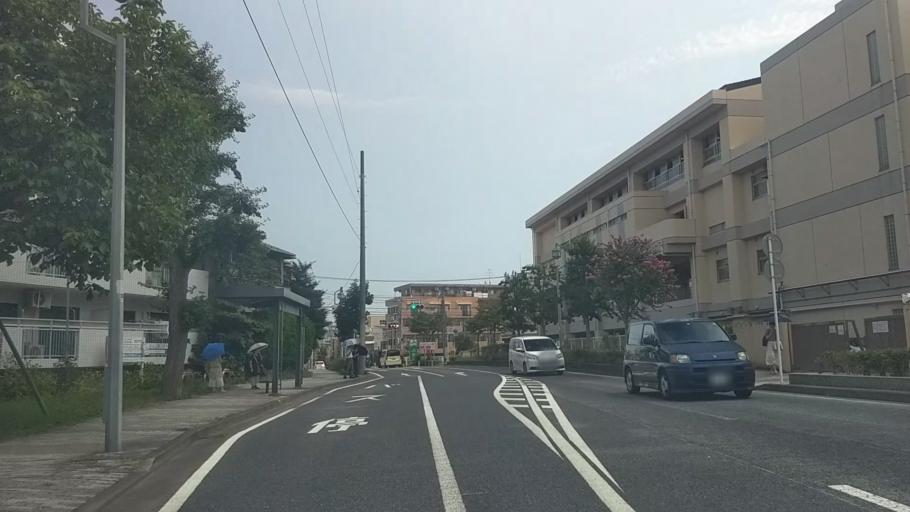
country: JP
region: Kanagawa
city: Yokohama
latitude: 35.4883
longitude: 139.6089
